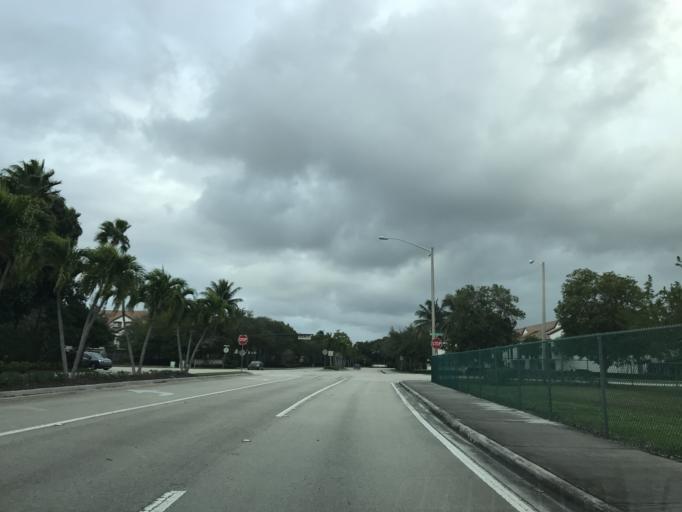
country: US
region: Florida
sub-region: Broward County
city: Coral Springs
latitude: 26.2975
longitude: -80.2829
